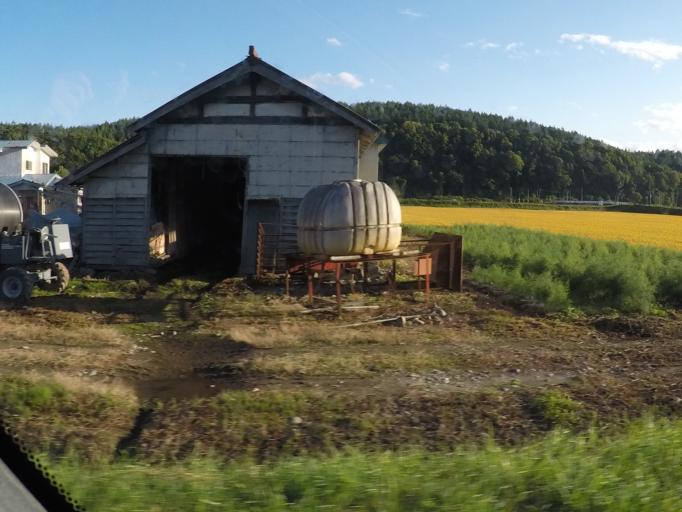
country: JP
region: Hokkaido
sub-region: Asahikawa-shi
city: Asahikawa
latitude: 43.6250
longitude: 142.5031
